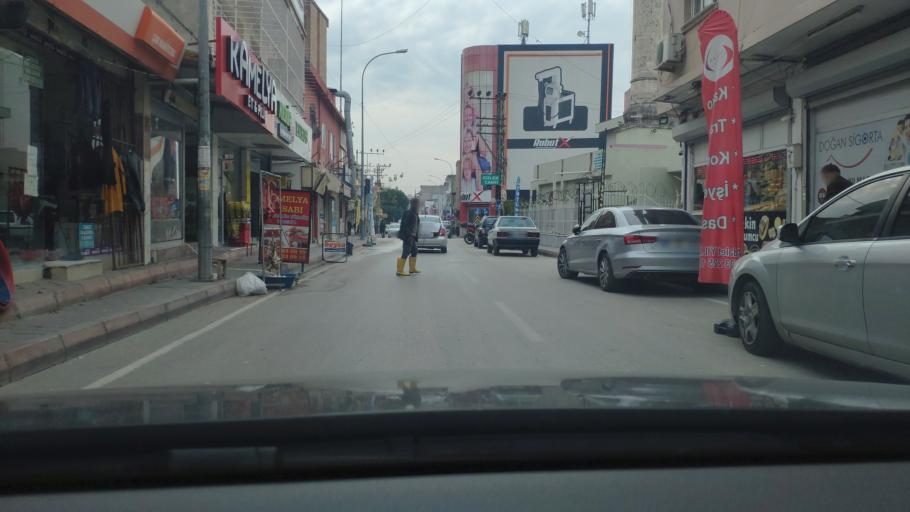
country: TR
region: Adana
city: Adana
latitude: 37.0152
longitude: 35.3145
